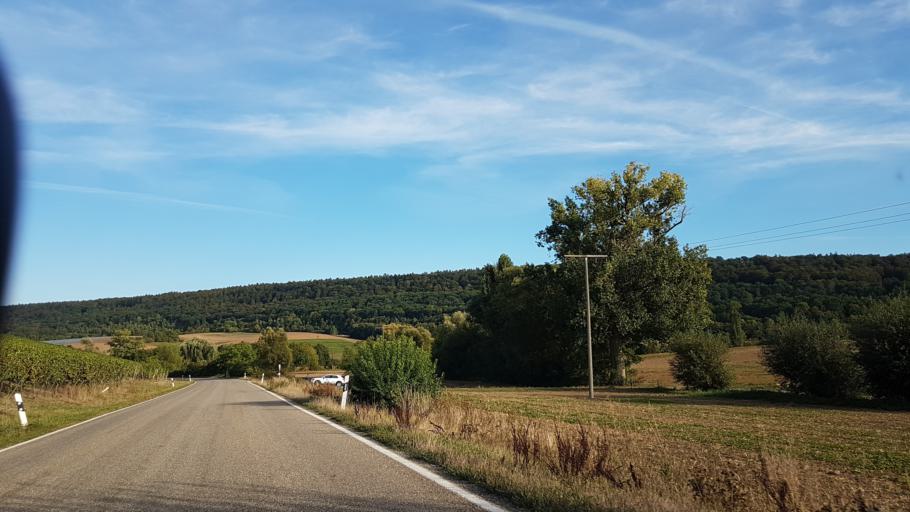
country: DE
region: Baden-Wuerttemberg
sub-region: Regierungsbezirk Stuttgart
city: Eberstadt
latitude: 49.1764
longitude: 9.3065
